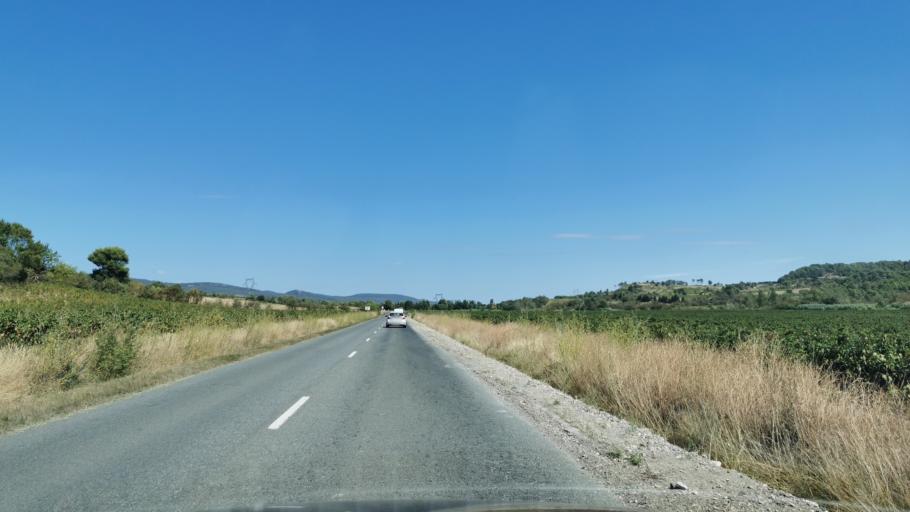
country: FR
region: Languedoc-Roussillon
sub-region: Departement de l'Aude
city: Conques-sur-Orbiel
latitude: 43.2948
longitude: 2.4533
